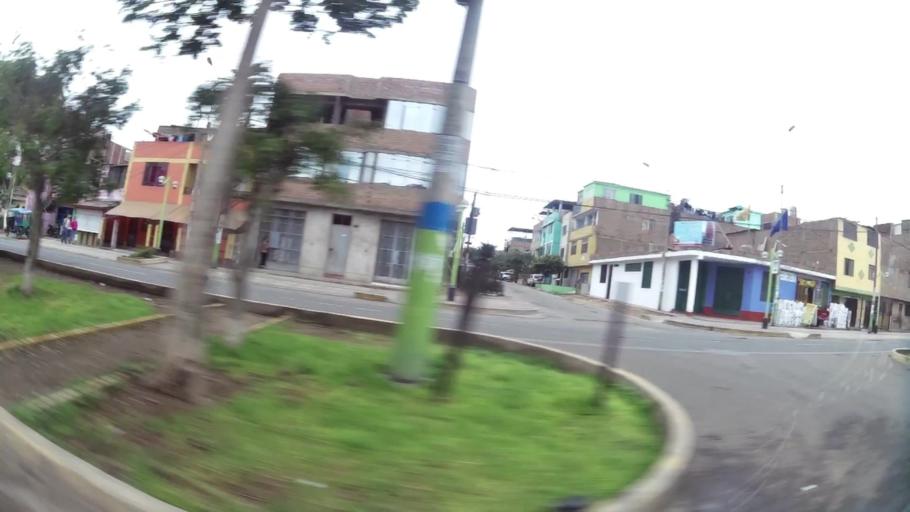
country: PE
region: Lima
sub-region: Lima
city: Vitarte
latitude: -12.0390
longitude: -76.9649
